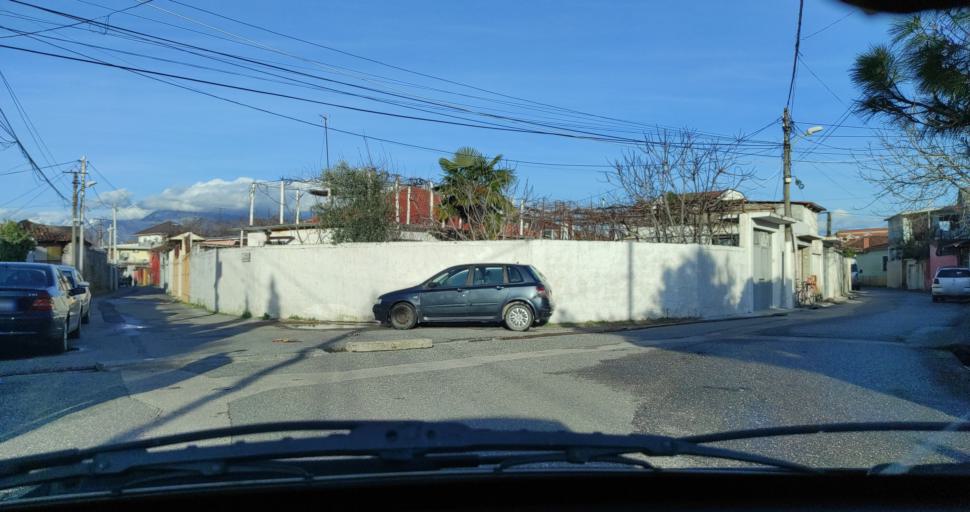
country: AL
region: Shkoder
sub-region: Rrethi i Shkodres
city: Shkoder
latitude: 42.0761
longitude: 19.5048
